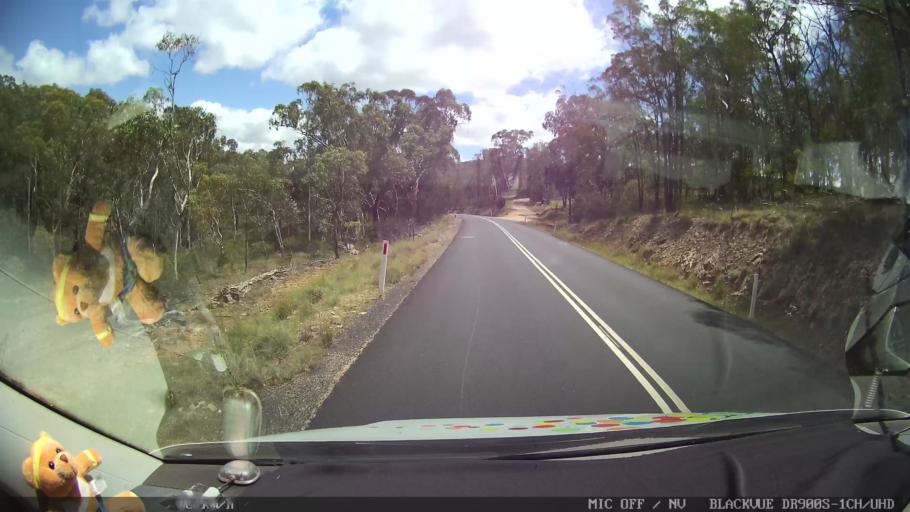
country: AU
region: New South Wales
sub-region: Glen Innes Severn
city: Glen Innes
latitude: -29.5660
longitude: 151.6687
